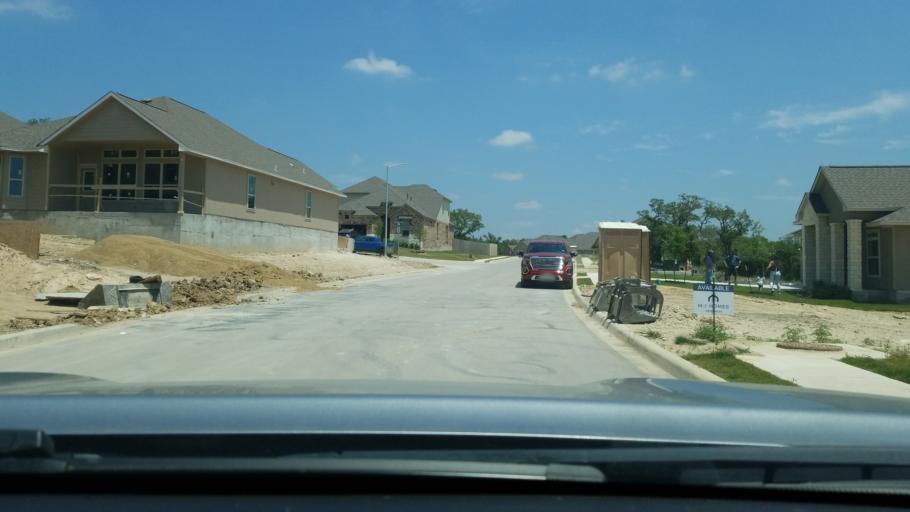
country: US
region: Texas
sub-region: Comal County
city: Bulverde
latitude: 29.7992
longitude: -98.5227
